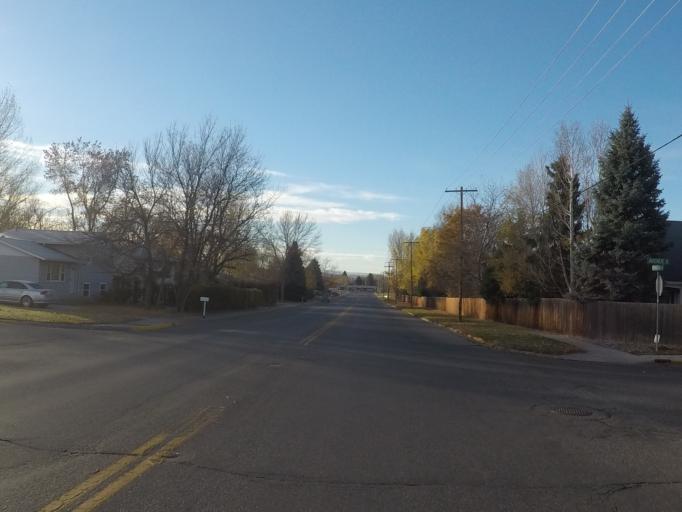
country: US
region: Montana
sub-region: Yellowstone County
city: Billings
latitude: 45.7879
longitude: -108.5903
